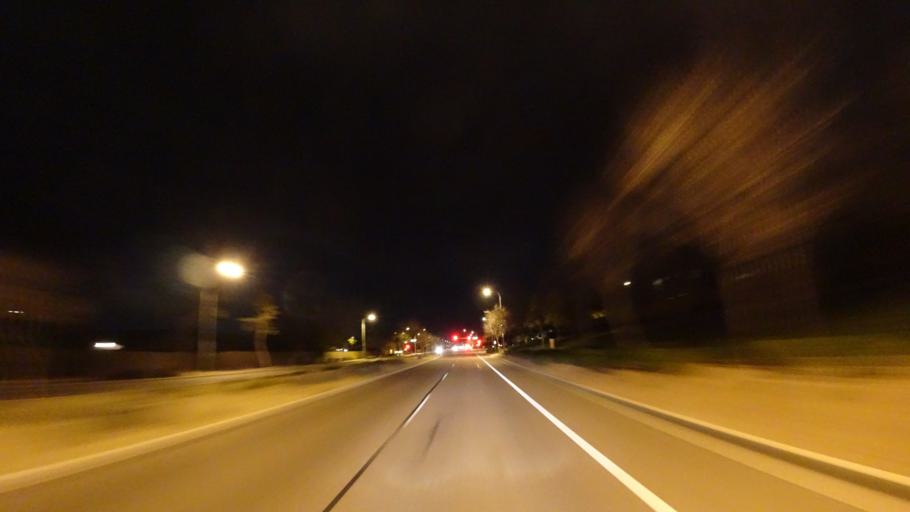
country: US
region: Arizona
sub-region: Maricopa County
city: Sun Lakes
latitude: 33.2474
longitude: -111.8519
